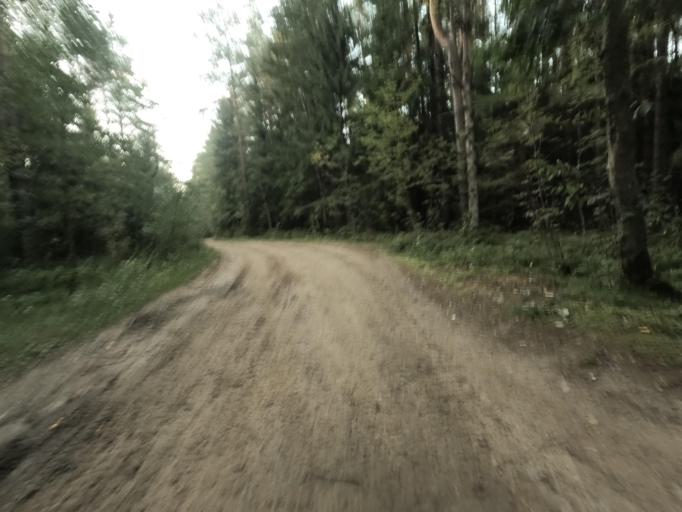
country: RU
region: Leningrad
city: Otradnoye
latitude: 59.8515
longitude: 30.7964
